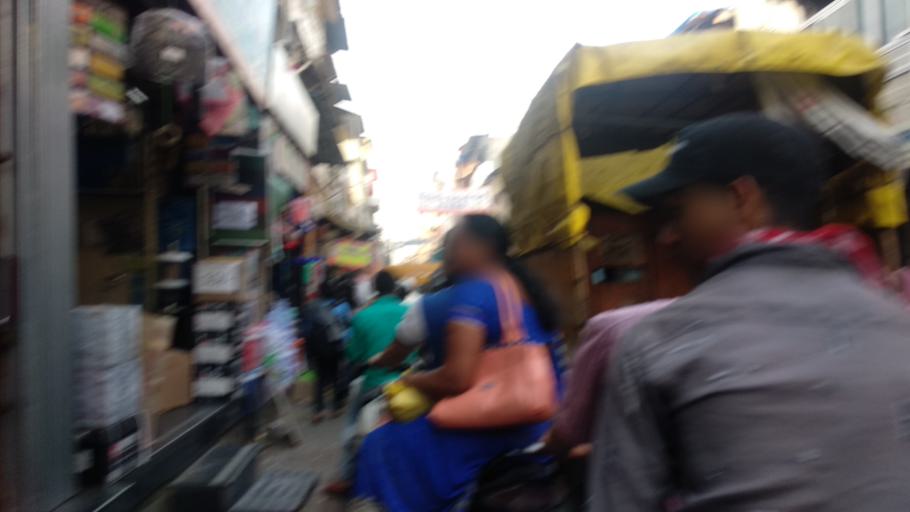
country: IN
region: Maharashtra
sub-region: Pune Division
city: Pune
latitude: 18.5133
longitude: 73.8596
